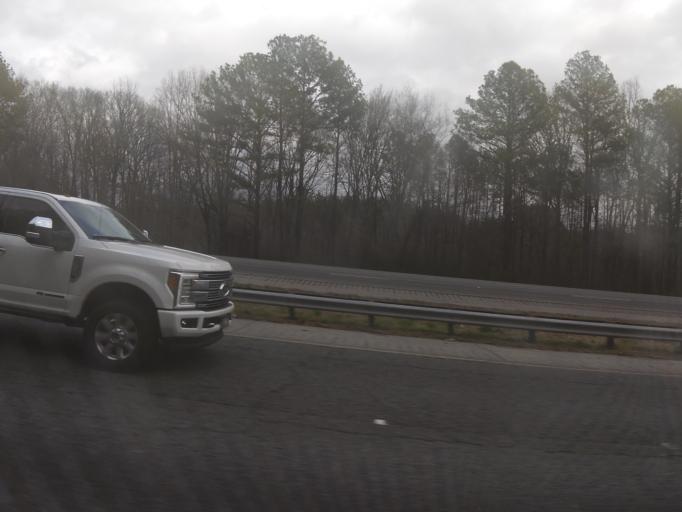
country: US
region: Georgia
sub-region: Gordon County
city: Calhoun
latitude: 34.6135
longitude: -84.9632
